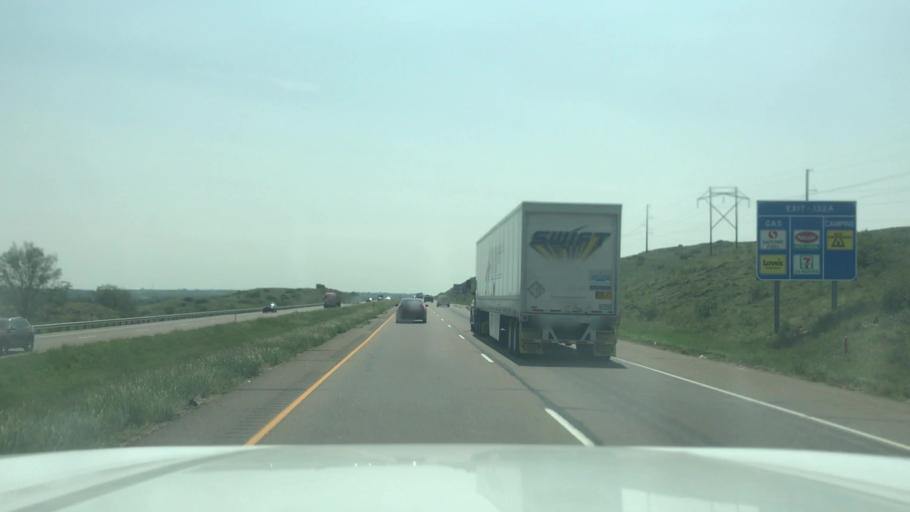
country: US
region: Colorado
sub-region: El Paso County
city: Security-Widefield
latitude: 38.7380
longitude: -104.7464
